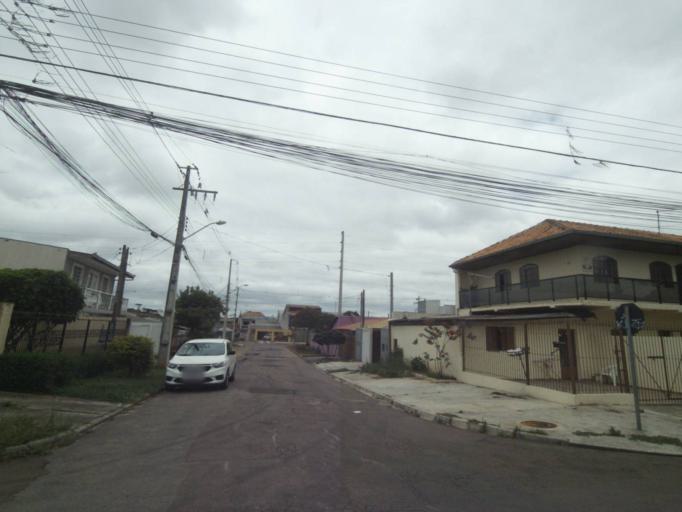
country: BR
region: Parana
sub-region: Sao Jose Dos Pinhais
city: Sao Jose dos Pinhais
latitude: -25.5507
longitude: -49.2592
